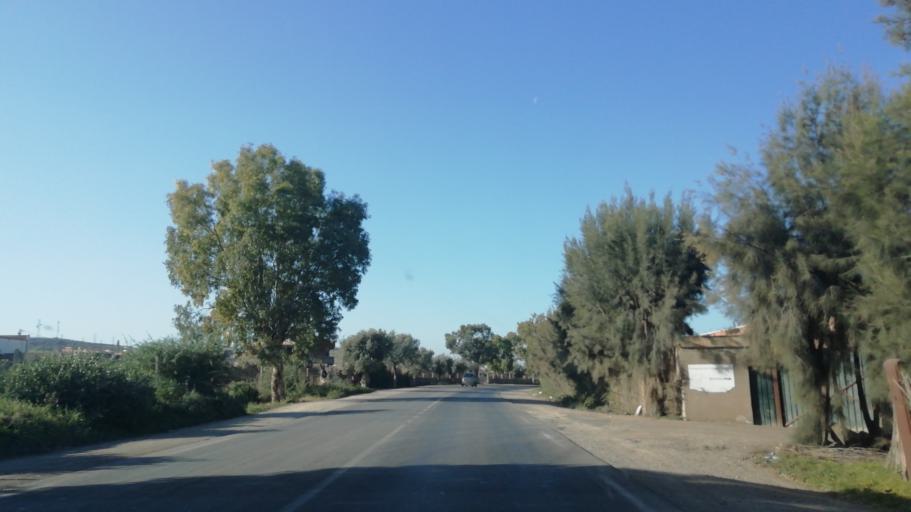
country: DZ
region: Mascara
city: Mascara
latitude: 35.6292
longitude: 0.1284
